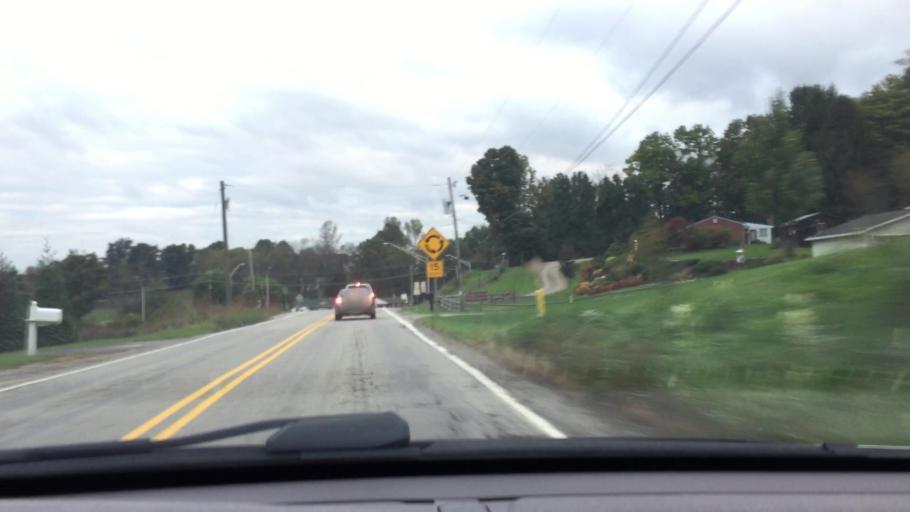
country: US
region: Pennsylvania
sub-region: Washington County
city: McMurray
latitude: 40.2026
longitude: -80.1248
